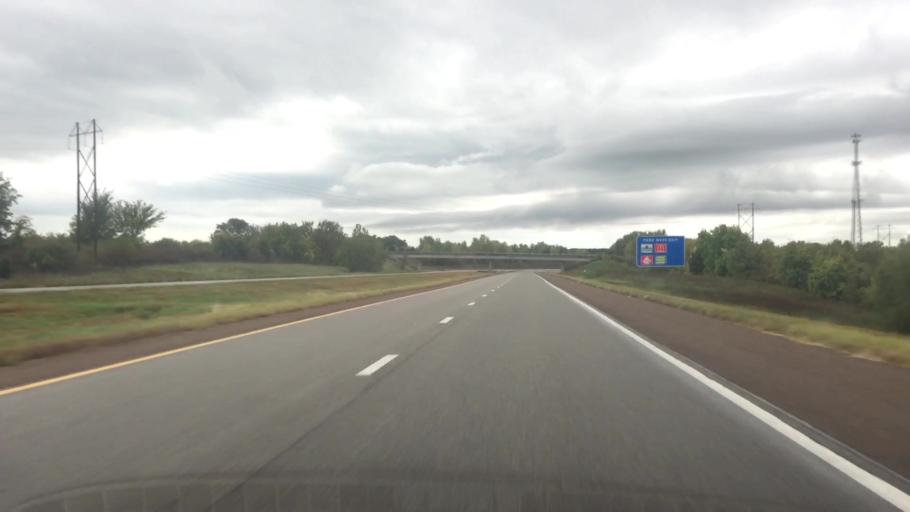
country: US
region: Kansas
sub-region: Miami County
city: Paola
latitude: 38.5885
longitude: -94.8354
